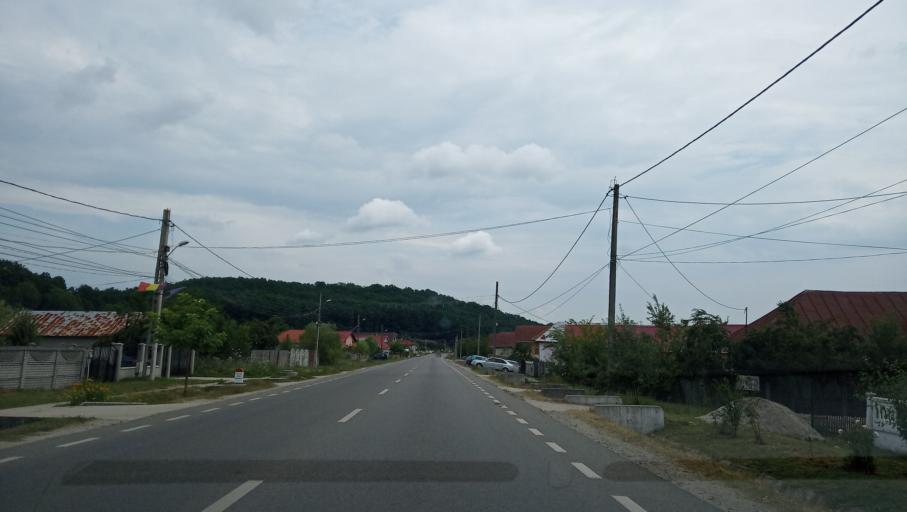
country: RO
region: Gorj
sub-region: Comuna Balteni
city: Balteni
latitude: 44.8602
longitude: 23.2840
